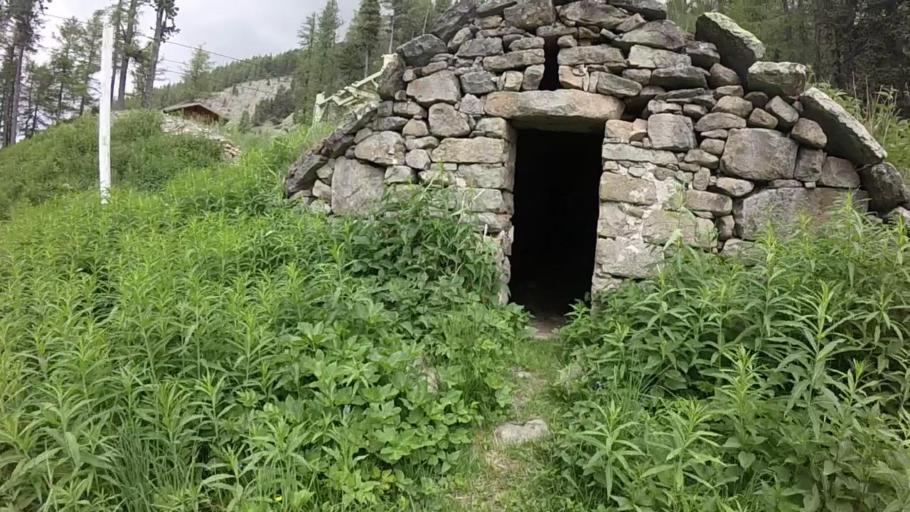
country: FR
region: Provence-Alpes-Cote d'Azur
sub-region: Departement des Alpes-de-Haute-Provence
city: Seyne-les-Alpes
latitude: 44.4043
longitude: 6.3753
